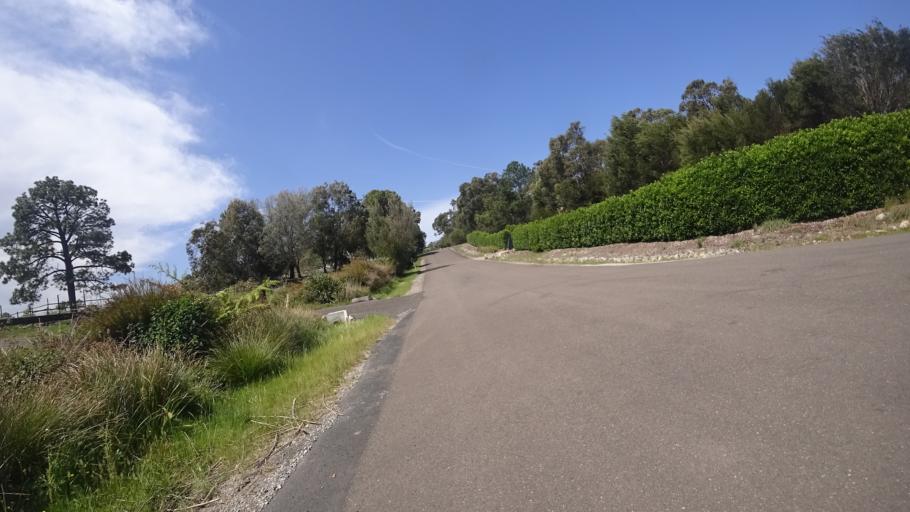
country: AU
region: New South Wales
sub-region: City of Sydney
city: North Turramurra
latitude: -33.6749
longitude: 151.1809
